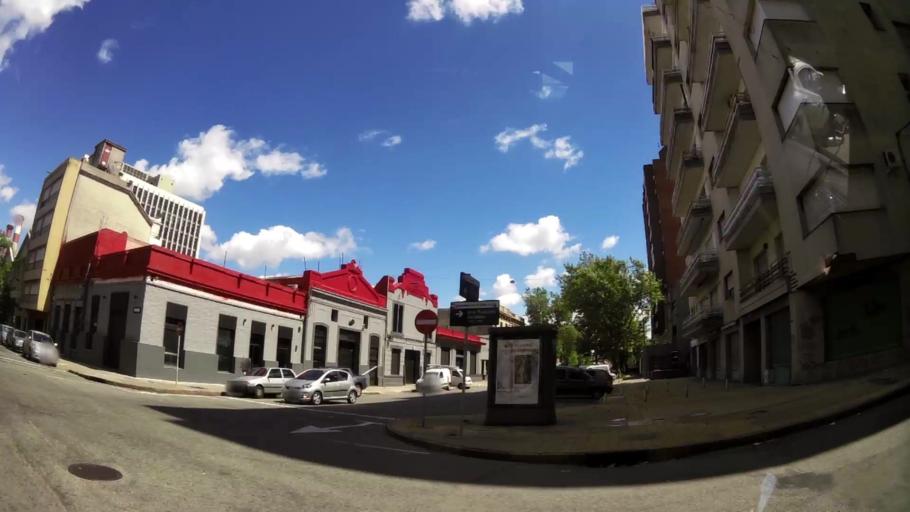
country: UY
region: Montevideo
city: Montevideo
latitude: -34.8858
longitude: -56.1935
